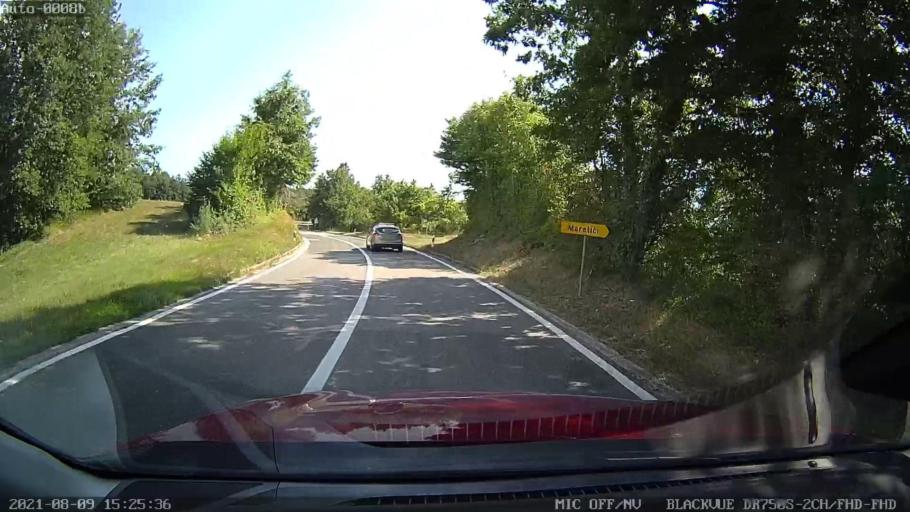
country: HR
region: Istarska
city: Pazin
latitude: 45.1681
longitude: 13.9086
